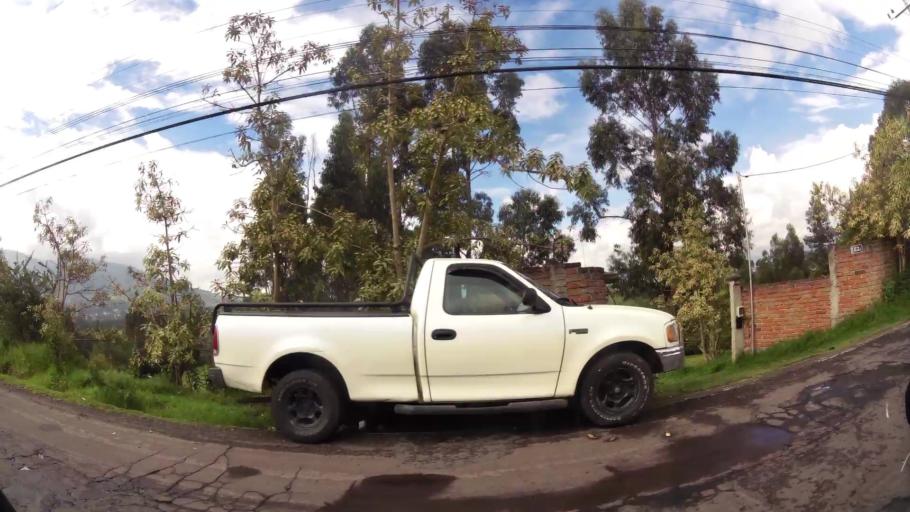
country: EC
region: Pichincha
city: Sangolqui
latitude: -0.3109
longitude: -78.4099
